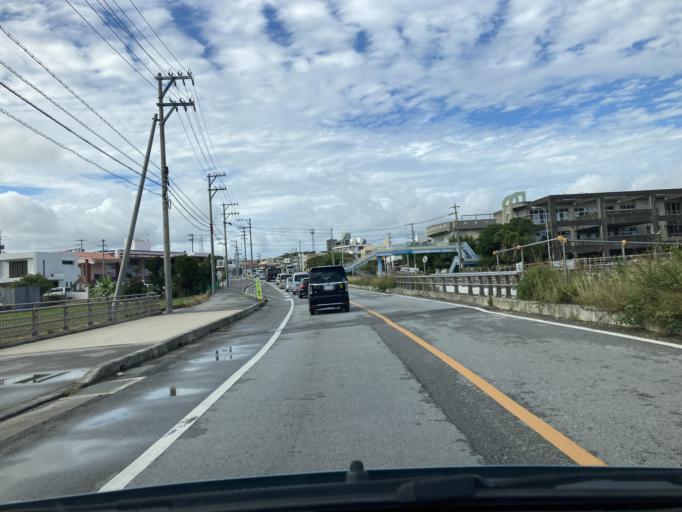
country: JP
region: Okinawa
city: Tomigusuku
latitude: 26.1506
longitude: 127.7234
